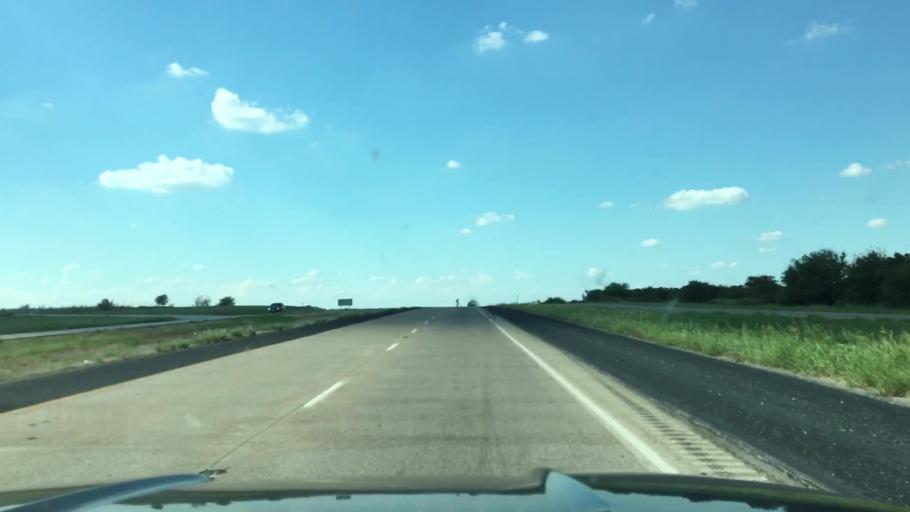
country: US
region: Texas
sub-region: Wise County
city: New Fairview
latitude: 33.1157
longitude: -97.4806
